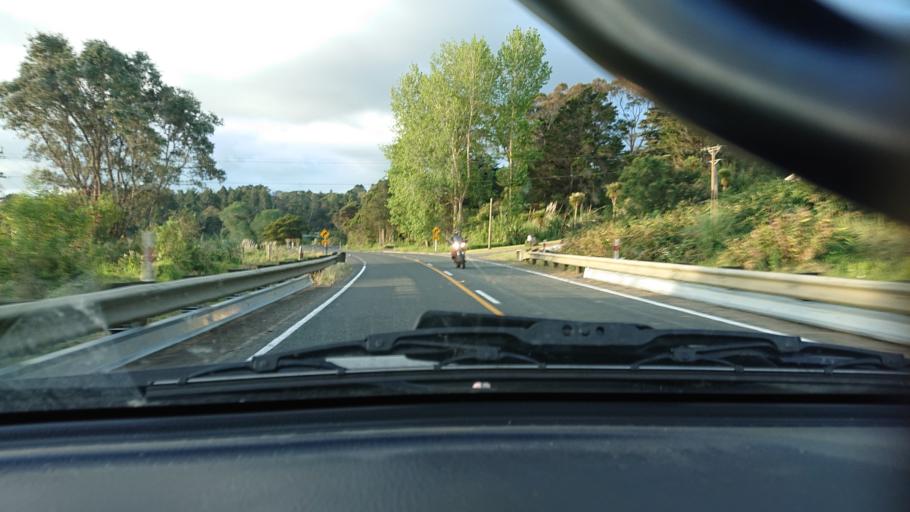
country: NZ
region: Auckland
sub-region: Auckland
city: Parakai
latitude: -36.5317
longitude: 174.4555
